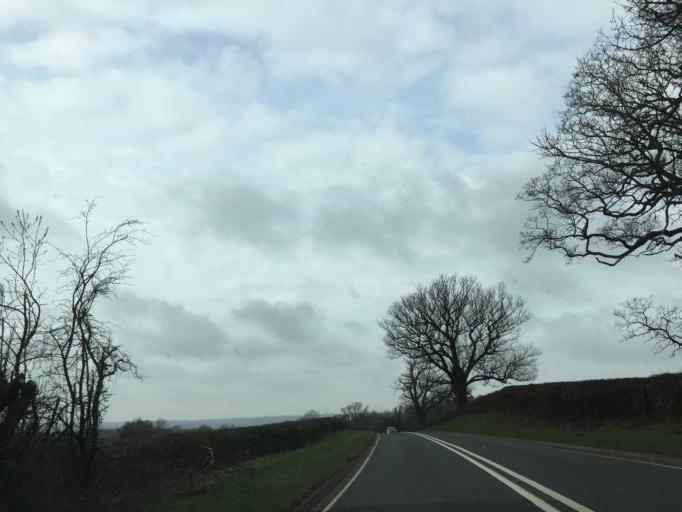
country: GB
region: England
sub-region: Warwickshire
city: Studley
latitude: 52.2994
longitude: -1.8703
